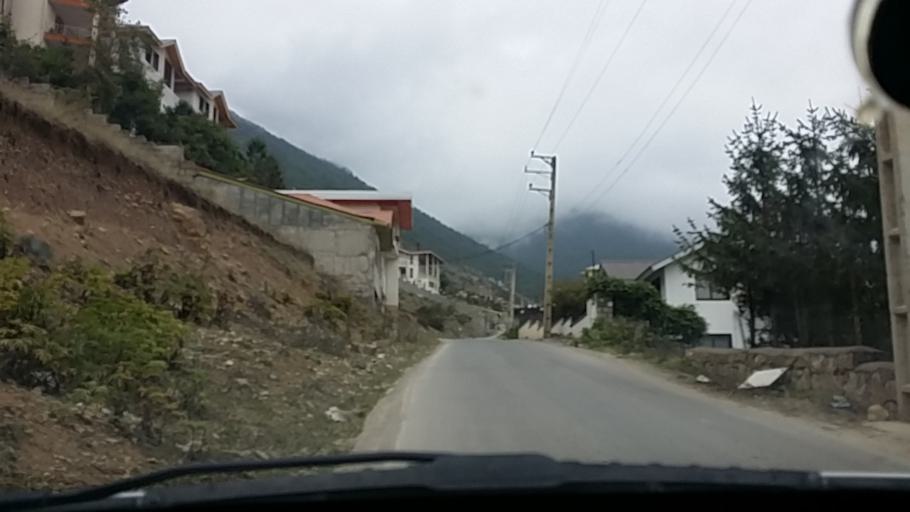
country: IR
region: Mazandaran
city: `Abbasabad
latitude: 36.4770
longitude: 51.1398
